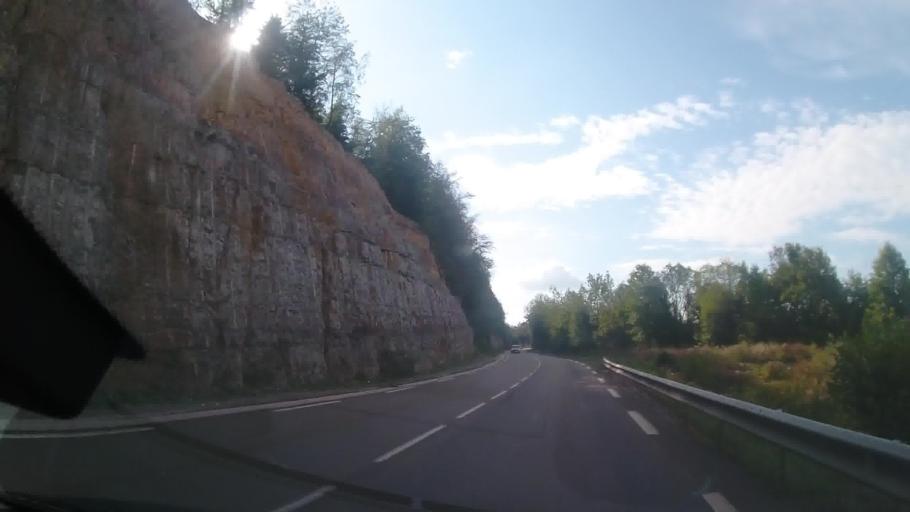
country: FR
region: Franche-Comte
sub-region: Departement du Jura
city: Clairvaux-les-Lacs
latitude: 46.5841
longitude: 5.8281
